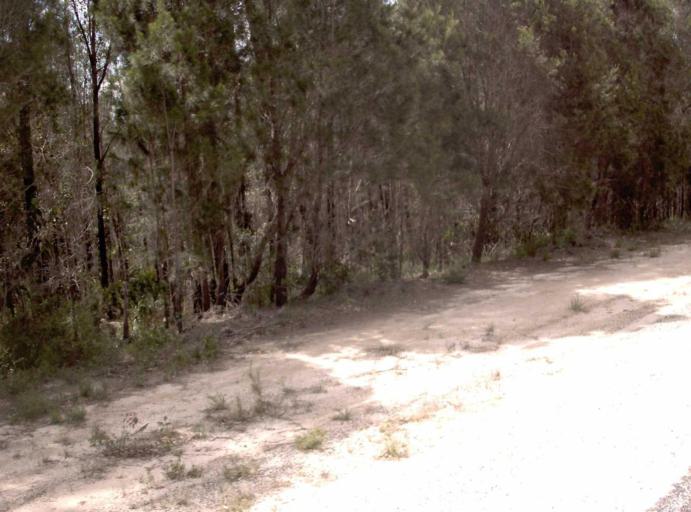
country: AU
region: New South Wales
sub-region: Bega Valley
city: Eden
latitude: -37.4115
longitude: 149.6556
